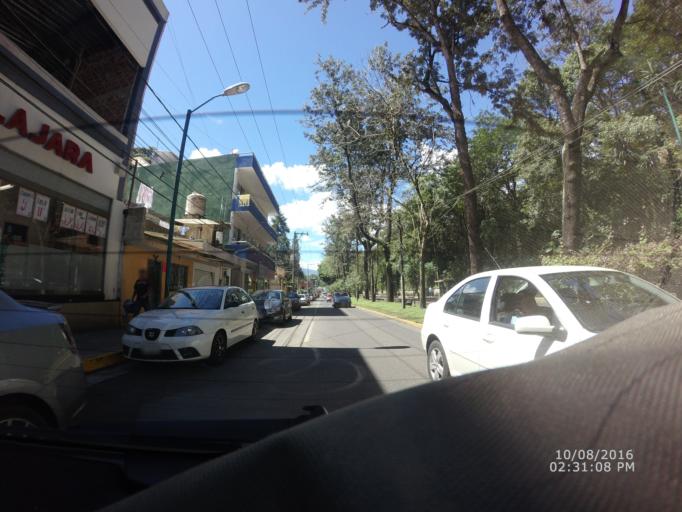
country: MX
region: Veracruz
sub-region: Xalapa
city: Lomas Verdes
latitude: 19.5129
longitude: -96.9071
